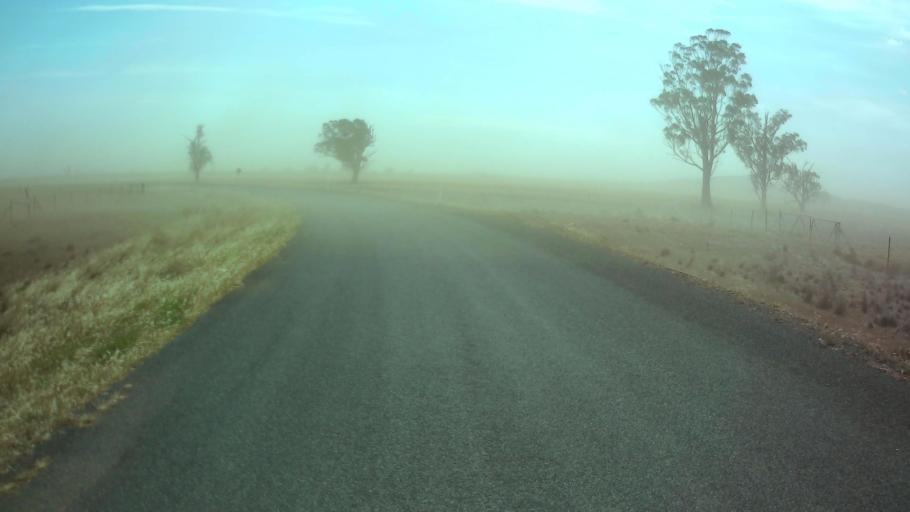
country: AU
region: New South Wales
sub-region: Weddin
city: Grenfell
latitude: -33.7364
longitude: 147.9963
